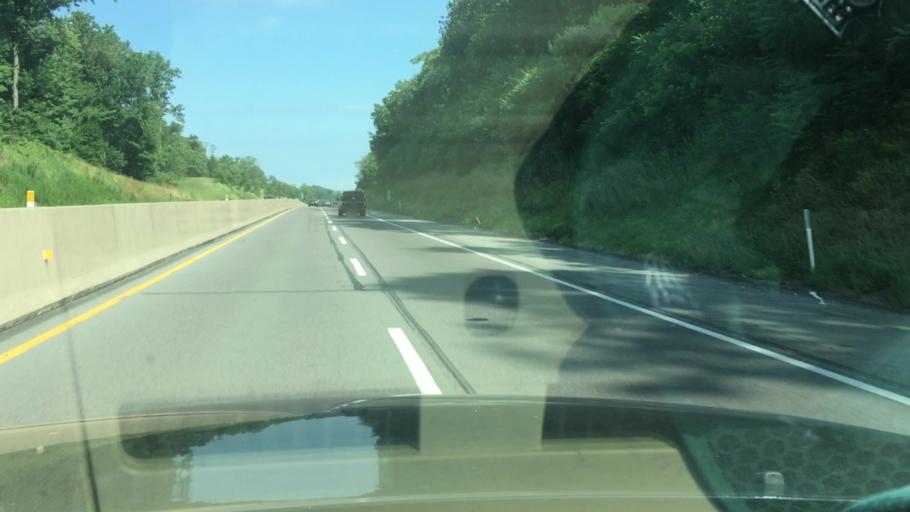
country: US
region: Pennsylvania
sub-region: Bucks County
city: Spinnerstown
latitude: 40.4740
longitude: -75.4558
